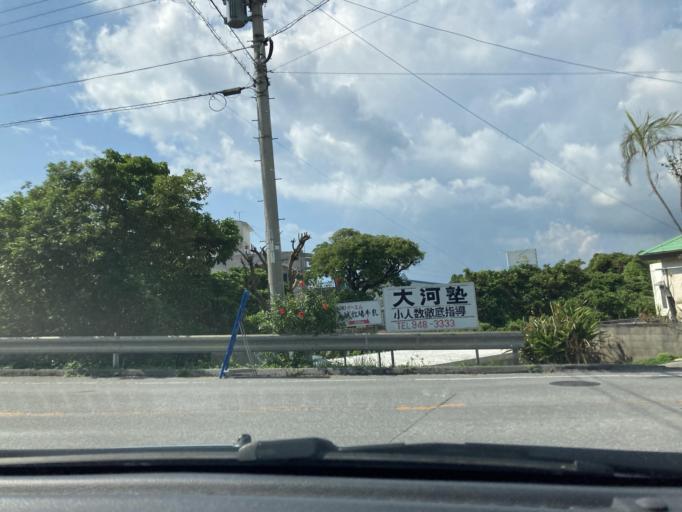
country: JP
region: Okinawa
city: Tomigusuku
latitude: 26.1412
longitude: 127.7678
